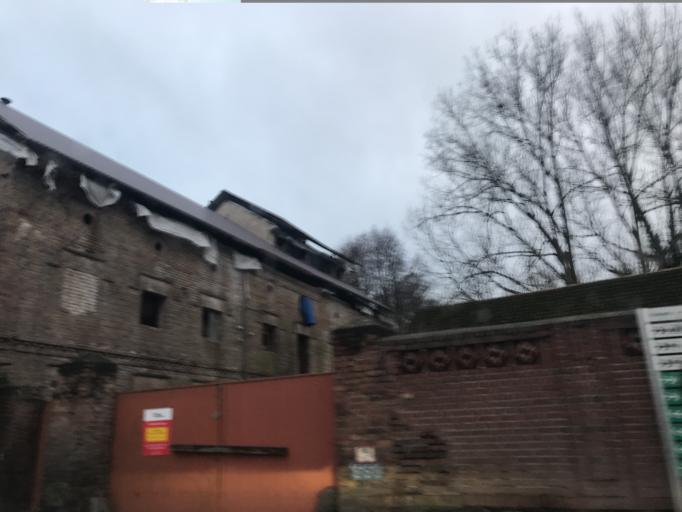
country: DE
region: Brandenburg
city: Rheinsberg
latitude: 53.0970
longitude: 12.8922
